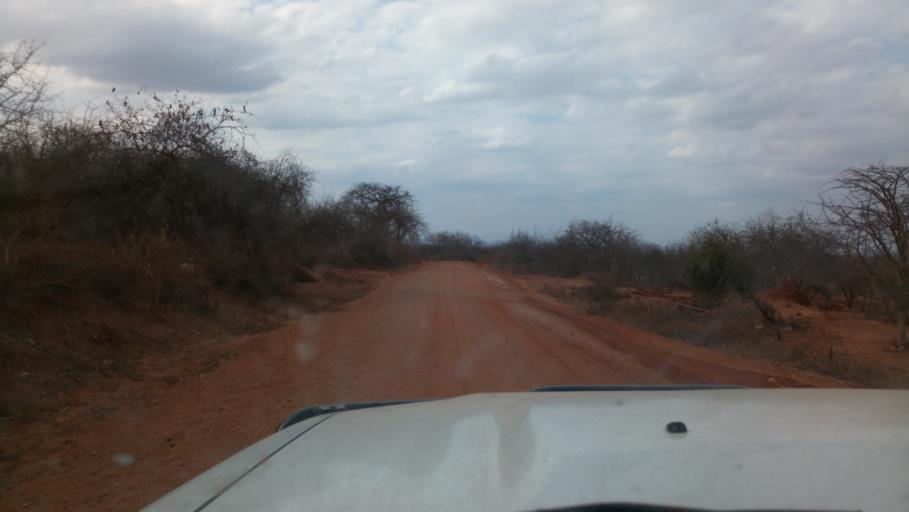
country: KE
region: Kitui
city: Kitui
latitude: -1.7673
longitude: 38.4405
